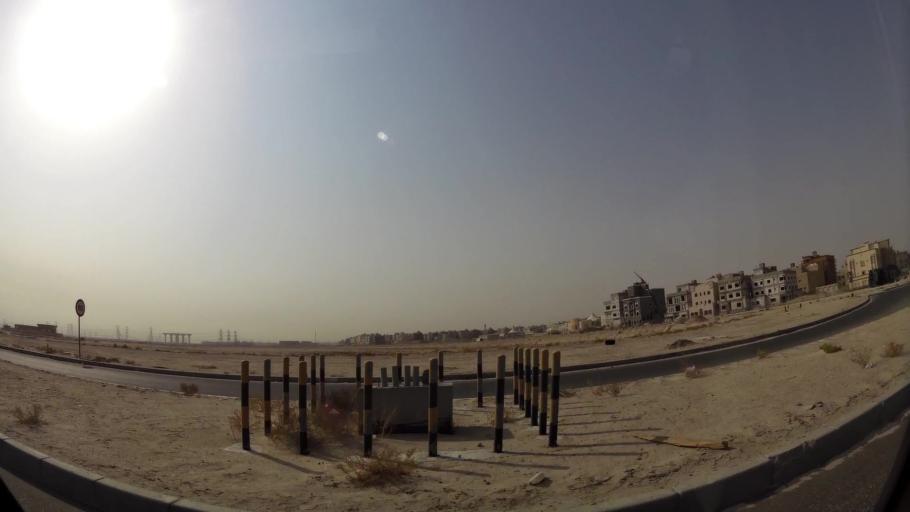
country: KW
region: Muhafazat al Jahra'
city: Al Jahra'
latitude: 29.3590
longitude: 47.7772
